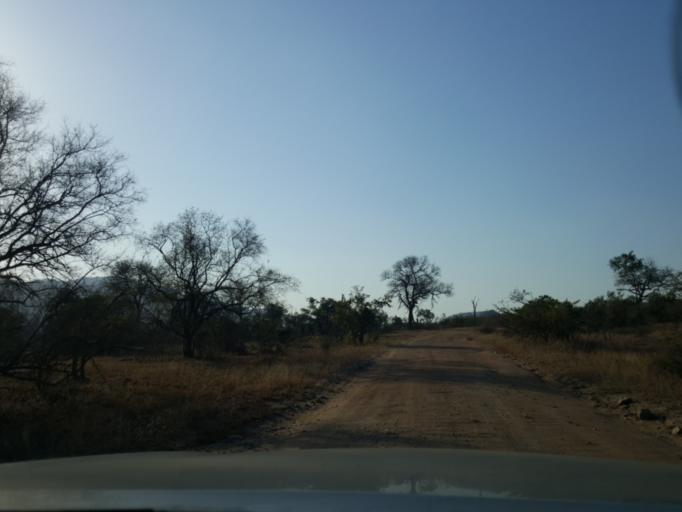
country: SZ
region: Hhohho
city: Ntfonjeni
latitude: -25.4126
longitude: 31.4406
